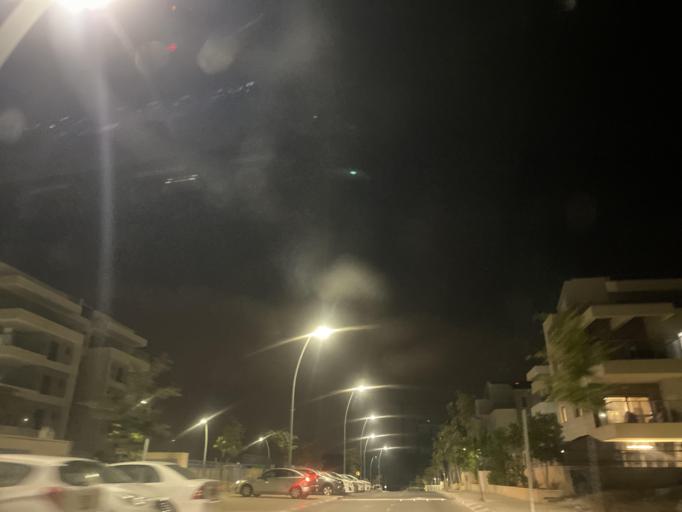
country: IL
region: Haifa
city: Daliyat el Karmil
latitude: 32.6371
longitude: 35.0765
